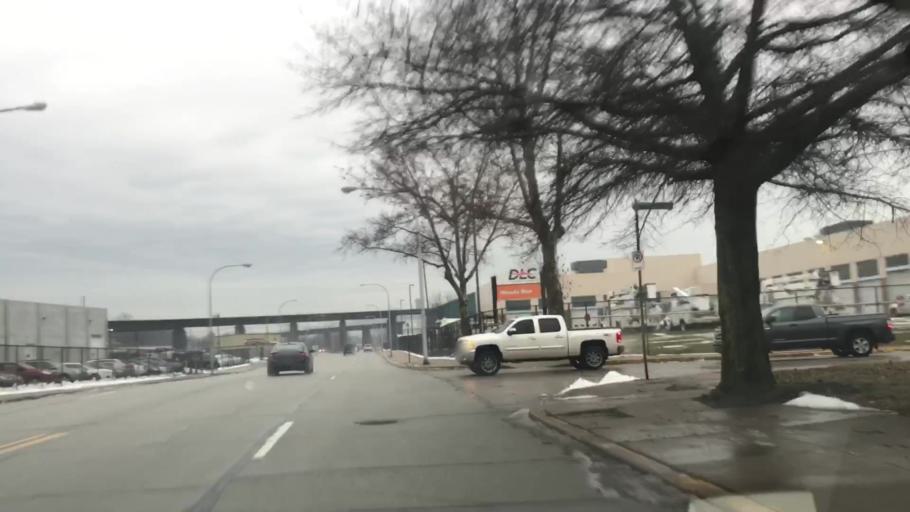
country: US
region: Pennsylvania
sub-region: Allegheny County
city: McKees Rocks
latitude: 40.4697
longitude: -80.0390
